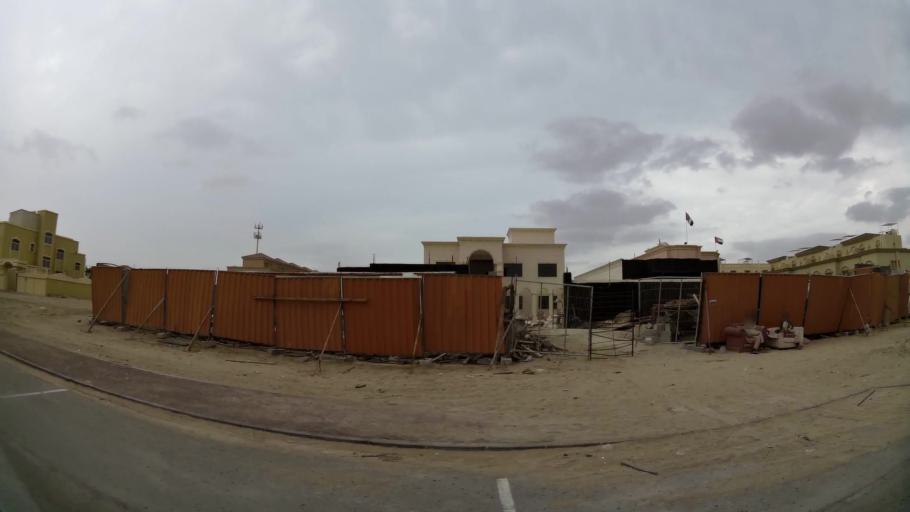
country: AE
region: Abu Dhabi
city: Abu Dhabi
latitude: 24.3714
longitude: 54.6480
